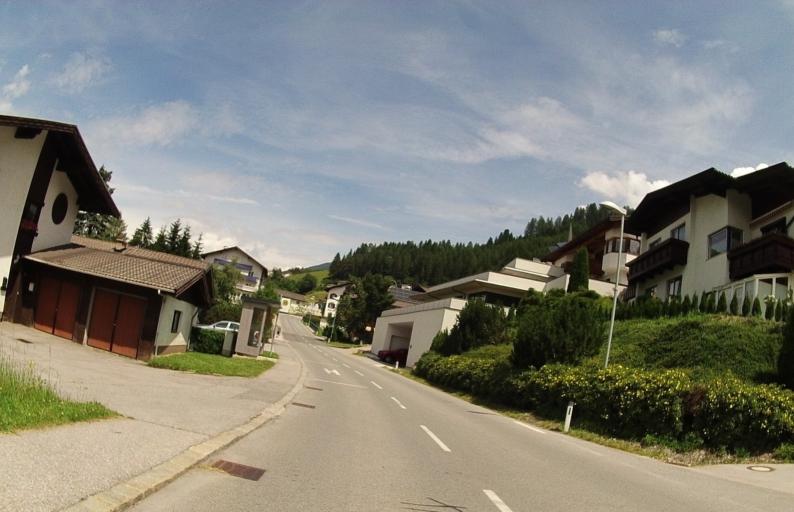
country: AT
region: Tyrol
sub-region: Politischer Bezirk Innsbruck Land
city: Pfons
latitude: 47.1401
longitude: 11.4605
